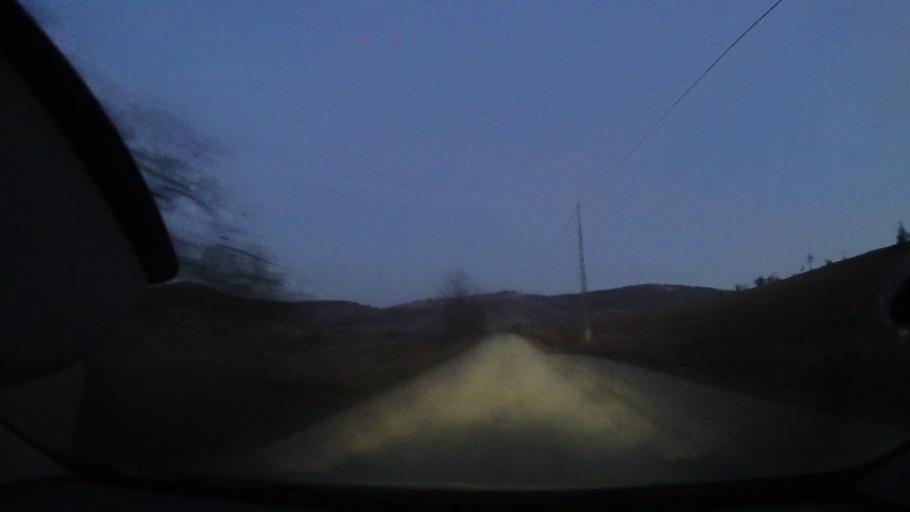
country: RO
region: Bihor
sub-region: Comuna Varciorog
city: Varciorog
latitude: 46.9897
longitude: 22.3259
